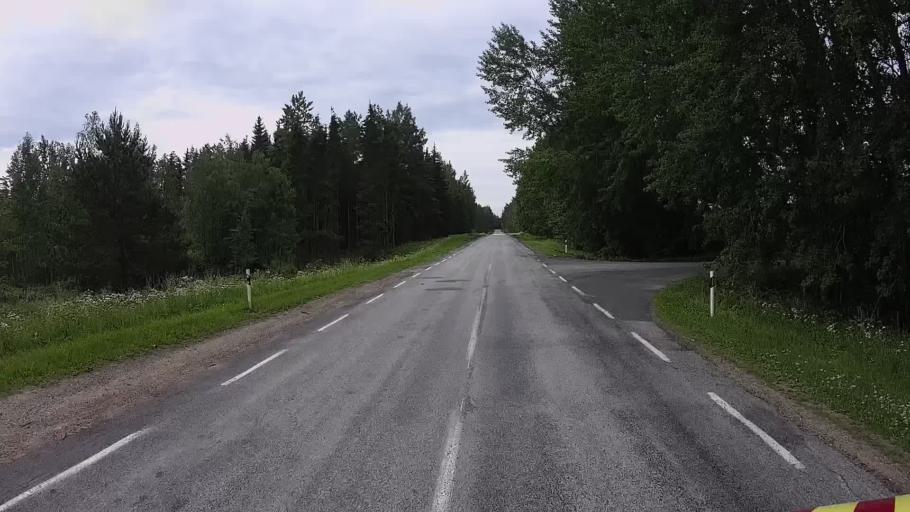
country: EE
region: Viljandimaa
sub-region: Karksi vald
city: Karksi-Nuia
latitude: 58.2177
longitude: 25.6190
